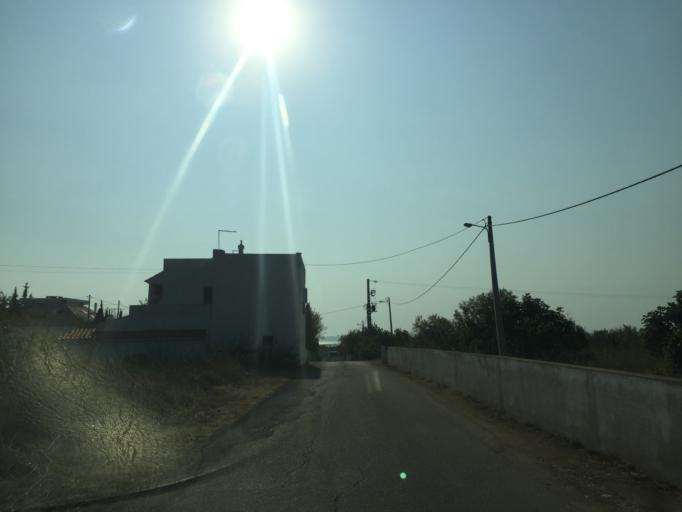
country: PT
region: Faro
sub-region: Albufeira
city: Guia
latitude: 37.0981
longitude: -8.2843
